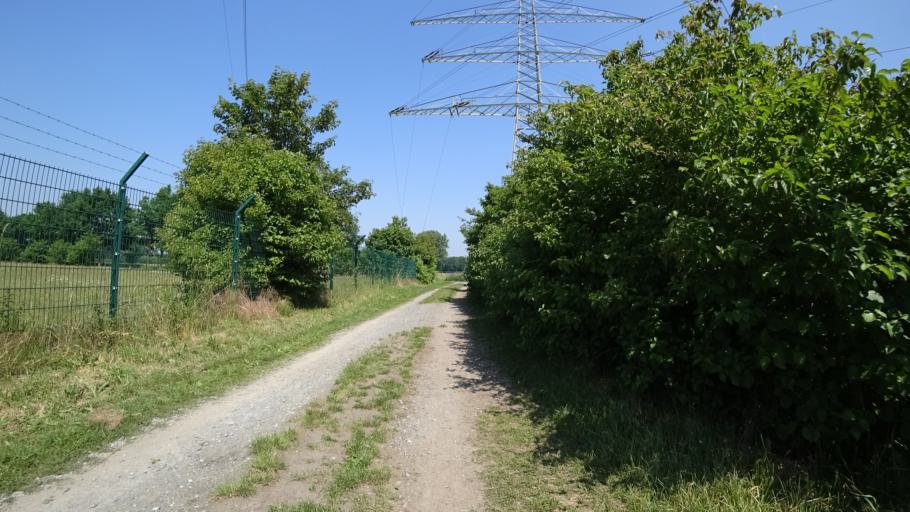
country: DE
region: North Rhine-Westphalia
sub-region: Regierungsbezirk Detmold
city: Guetersloh
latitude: 51.9358
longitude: 8.3677
